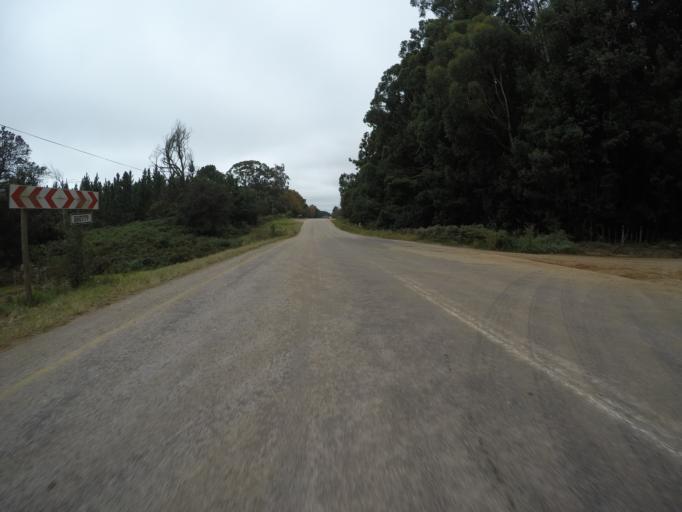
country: ZA
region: Eastern Cape
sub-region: Cacadu District Municipality
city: Kareedouw
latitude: -33.9943
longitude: 24.1156
